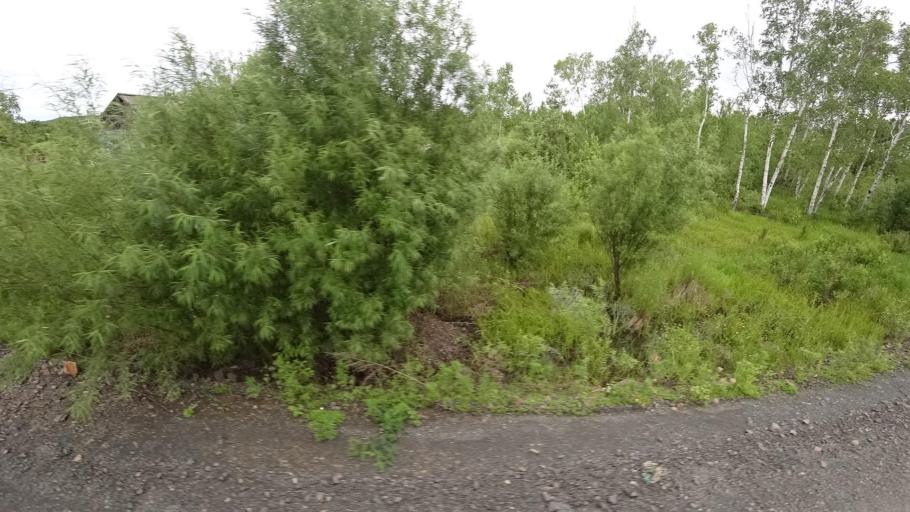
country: RU
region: Khabarovsk Krai
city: Amursk
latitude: 49.9009
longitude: 136.1361
